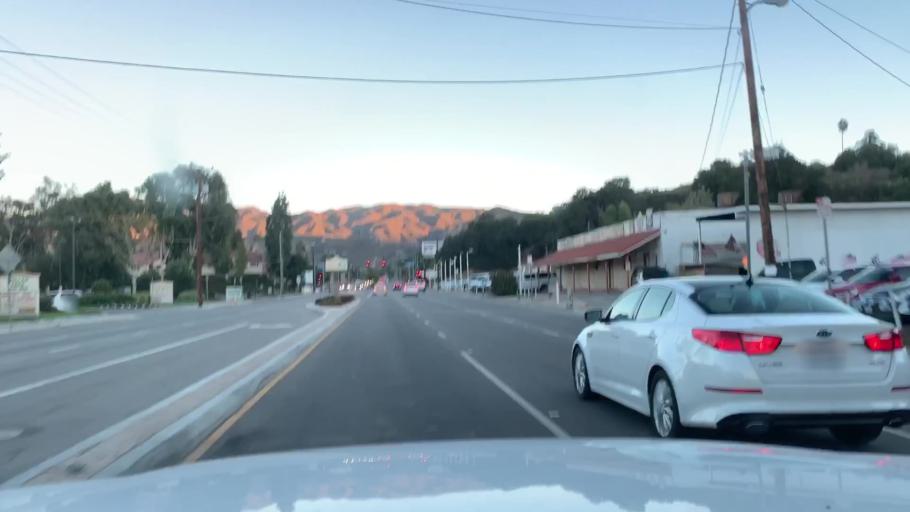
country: US
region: California
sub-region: Los Angeles County
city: Santa Clarita
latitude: 34.3719
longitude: -118.5166
